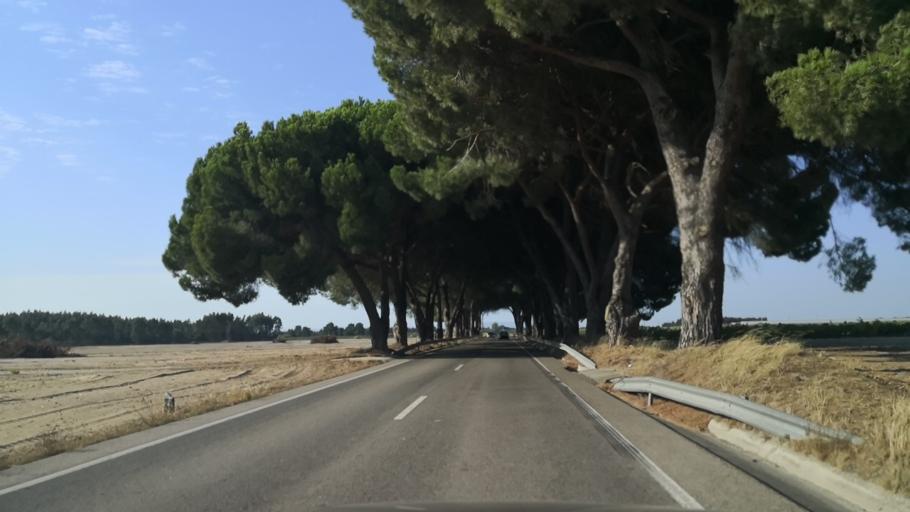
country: PT
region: Santarem
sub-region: Almeirim
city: Almeirim
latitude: 39.1607
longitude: -8.6204
